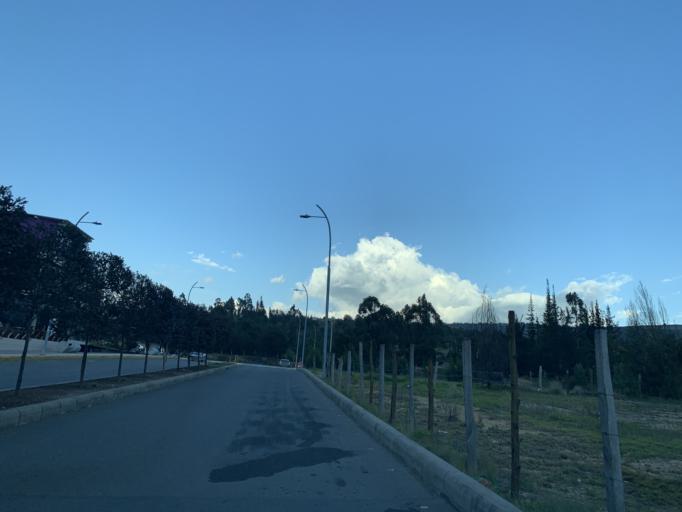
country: CO
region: Boyaca
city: Tunja
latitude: 5.5691
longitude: -73.3313
